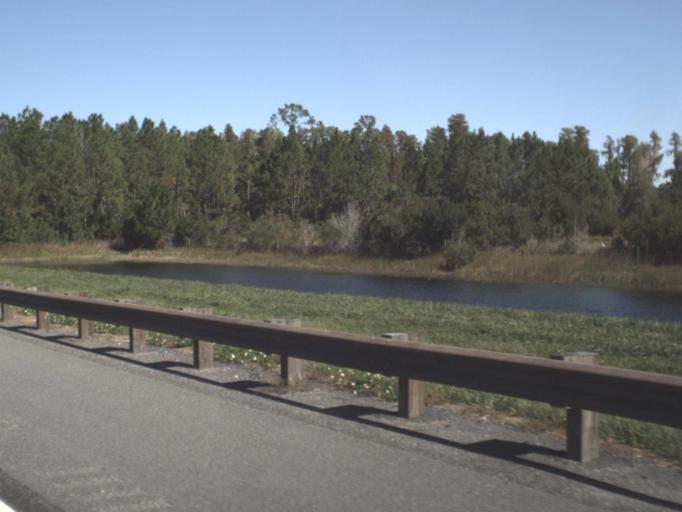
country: US
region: Florida
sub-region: Hillsborough County
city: Cheval
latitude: 28.1747
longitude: -82.5363
